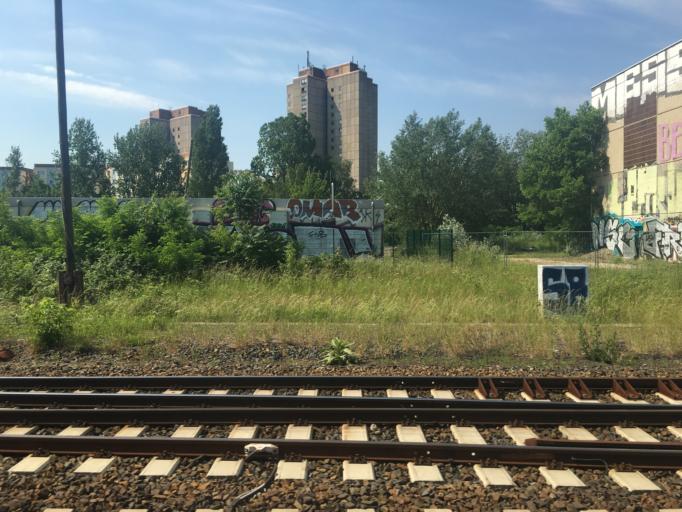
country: DE
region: Berlin
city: Prenzlauer Berg Bezirk
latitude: 52.5418
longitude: 13.4349
